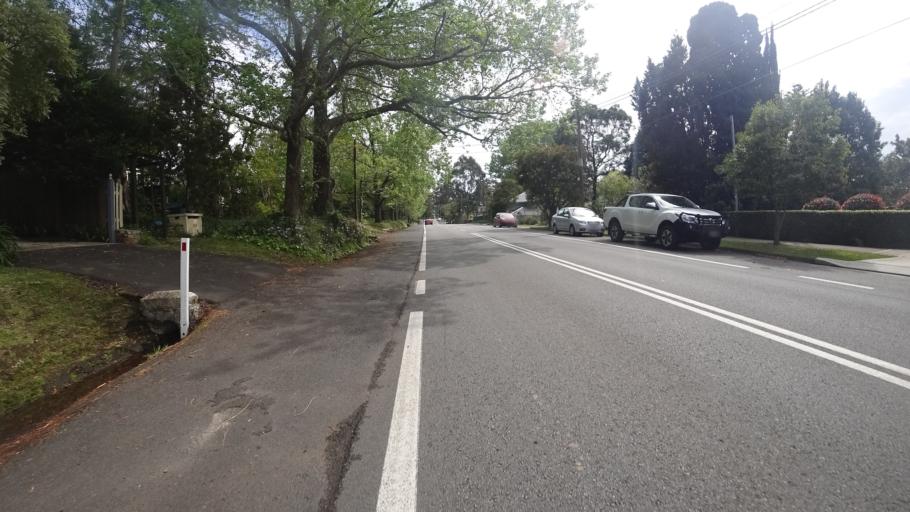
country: AU
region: New South Wales
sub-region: City of Sydney
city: North Turramurra
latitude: -33.7276
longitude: 151.1390
